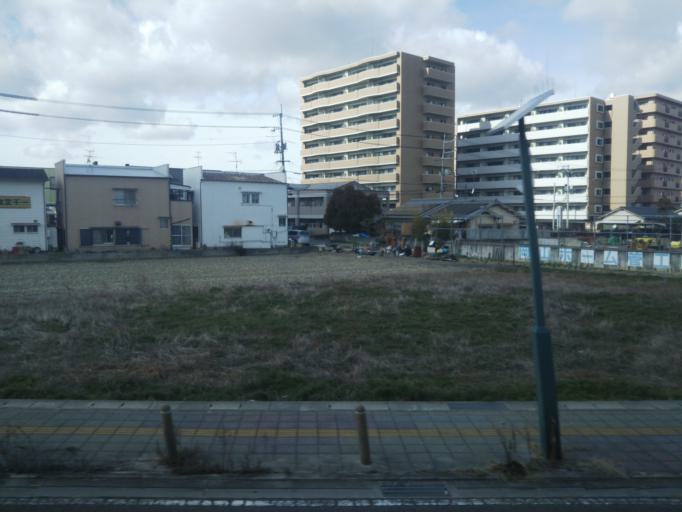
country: JP
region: Okayama
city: Okayama-shi
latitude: 34.6287
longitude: 133.8970
